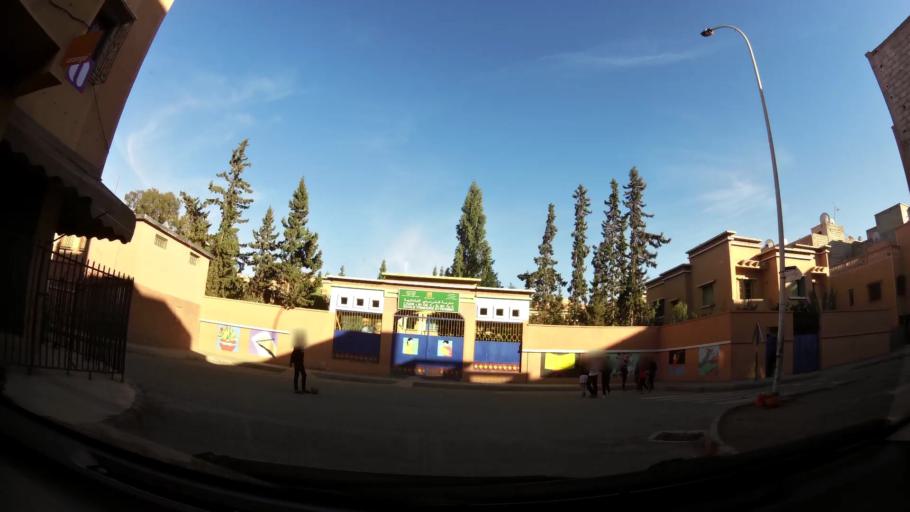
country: MA
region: Marrakech-Tensift-Al Haouz
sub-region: Marrakech
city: Marrakesh
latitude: 31.6197
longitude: -8.0646
